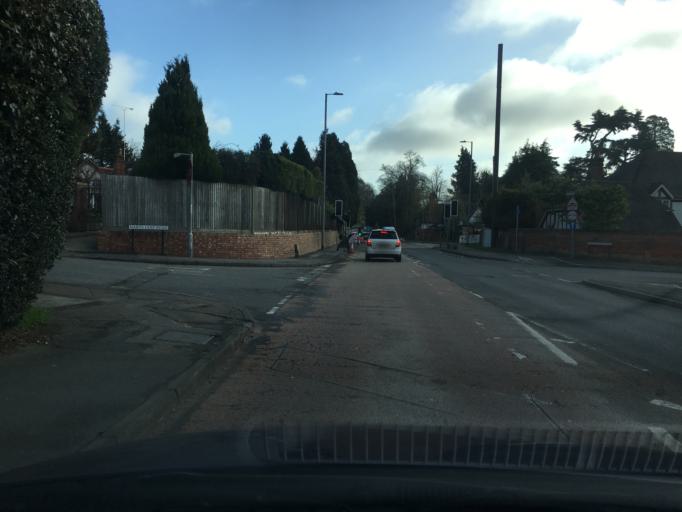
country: GB
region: England
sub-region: Bracknell Forest
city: Sandhurst
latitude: 51.3495
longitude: -0.8019
